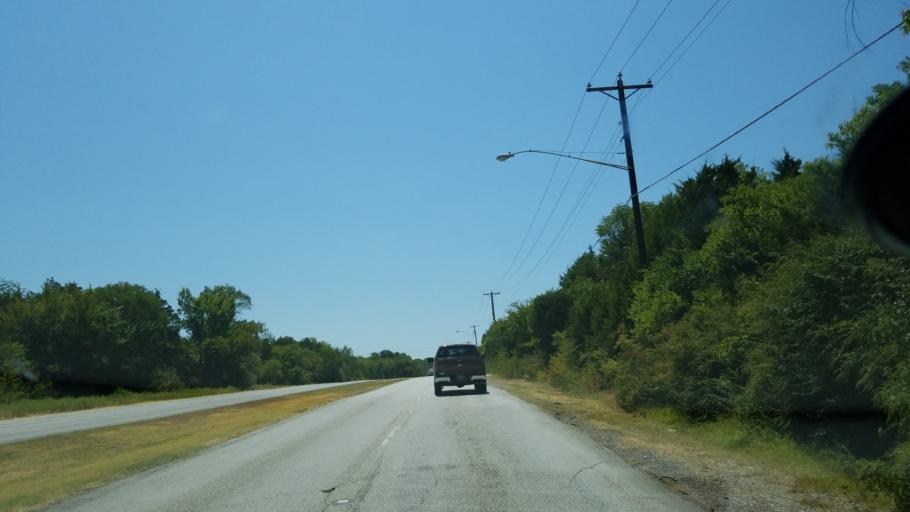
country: US
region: Texas
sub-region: Dallas County
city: Cockrell Hill
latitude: 32.7406
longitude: -96.9014
